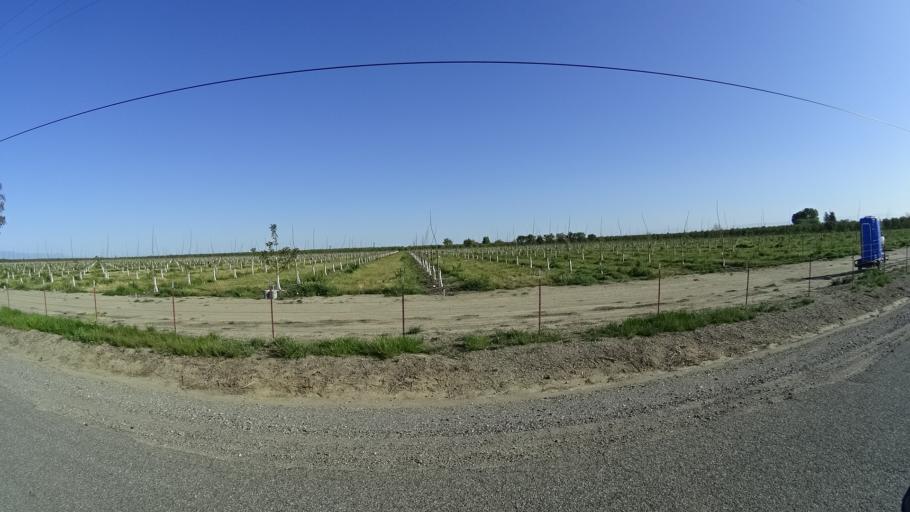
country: US
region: California
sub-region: Glenn County
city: Hamilton City
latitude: 39.6958
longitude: -122.0862
